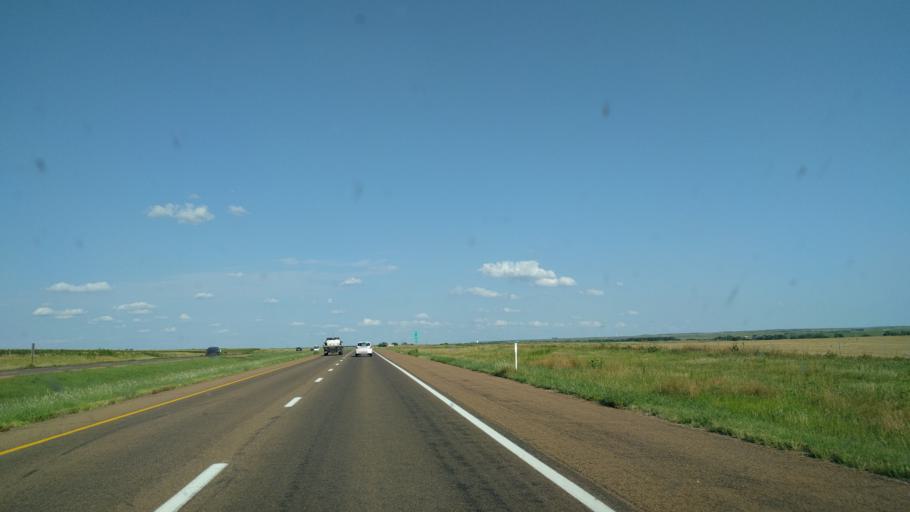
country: US
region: Kansas
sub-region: Ellis County
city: Ellis
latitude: 38.9476
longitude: -99.5173
